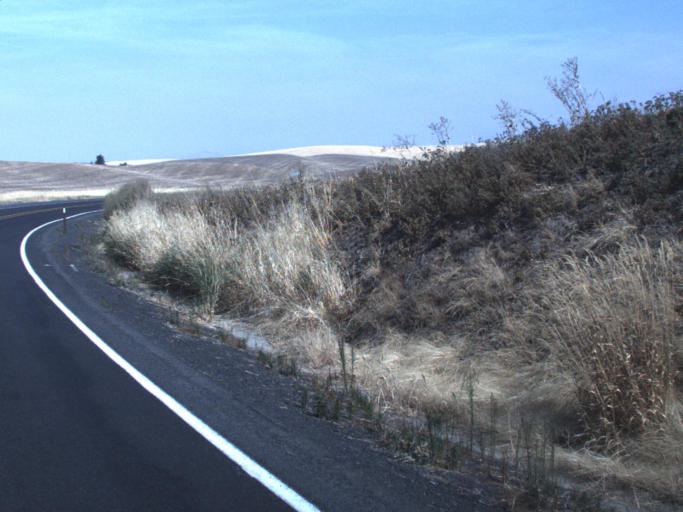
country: US
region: Washington
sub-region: Whitman County
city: Pullman
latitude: 46.9825
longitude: -117.1262
